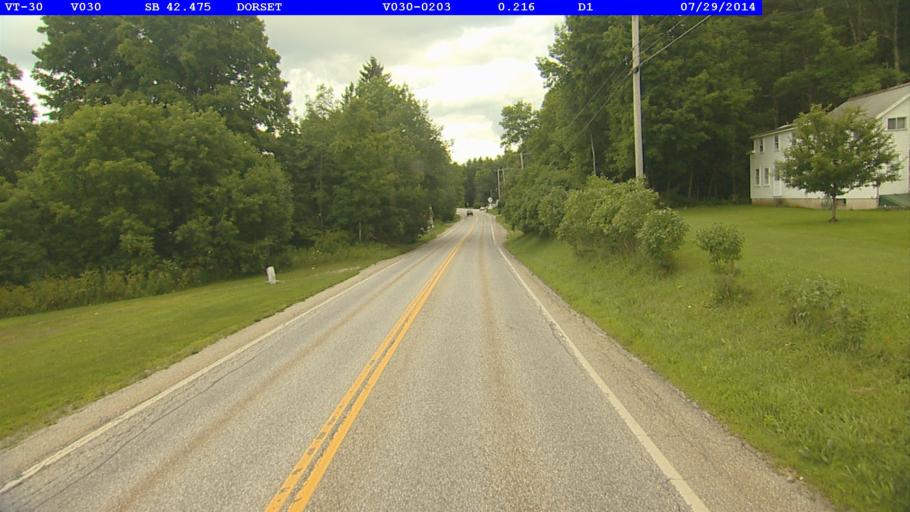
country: US
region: Vermont
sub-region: Bennington County
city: Manchester Center
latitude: 43.2153
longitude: -73.0691
